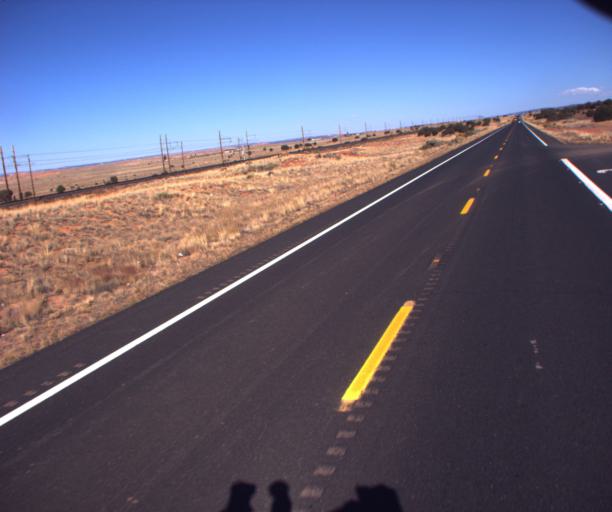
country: US
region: Arizona
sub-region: Coconino County
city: Kaibito
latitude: 36.4186
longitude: -110.8063
